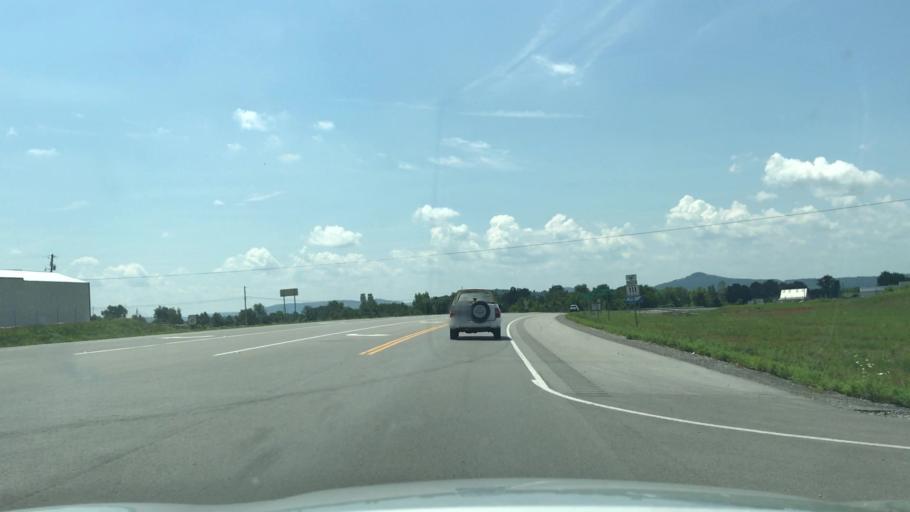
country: US
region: Tennessee
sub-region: Pickett County
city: Byrdstown
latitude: 36.6219
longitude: -85.0884
